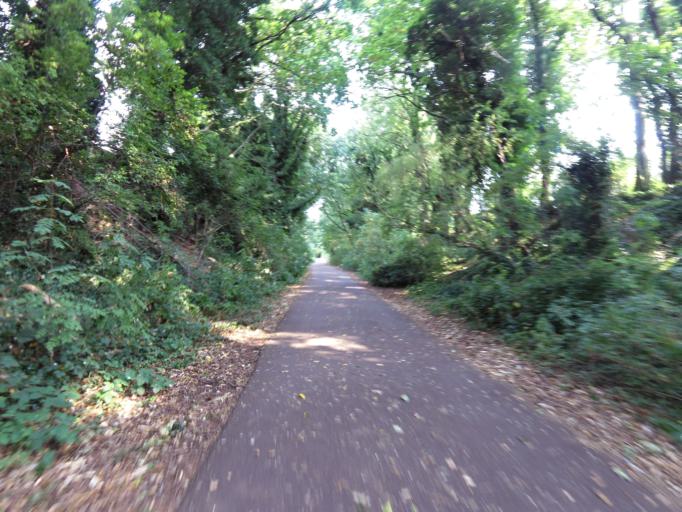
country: GB
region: England
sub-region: Hertfordshire
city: St Albans
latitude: 51.7500
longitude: -0.3046
